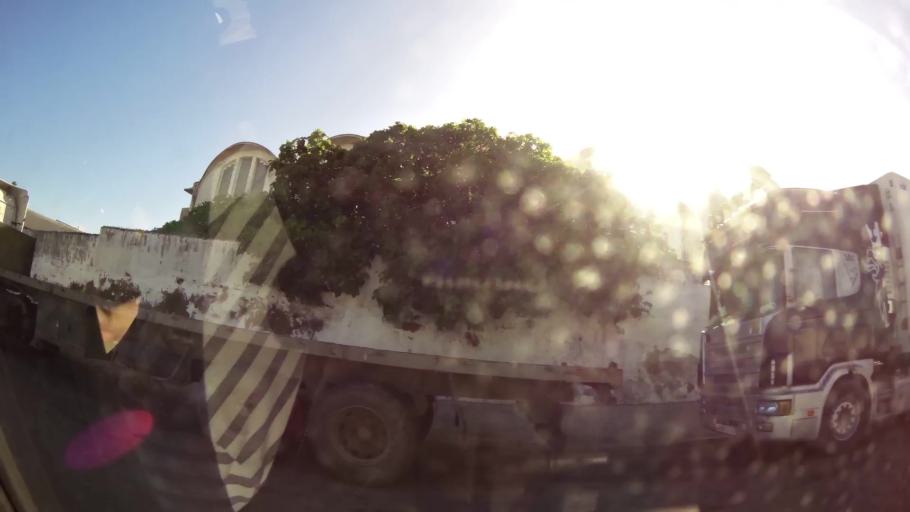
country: MA
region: Grand Casablanca
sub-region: Casablanca
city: Casablanca
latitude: 33.5996
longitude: -7.5726
